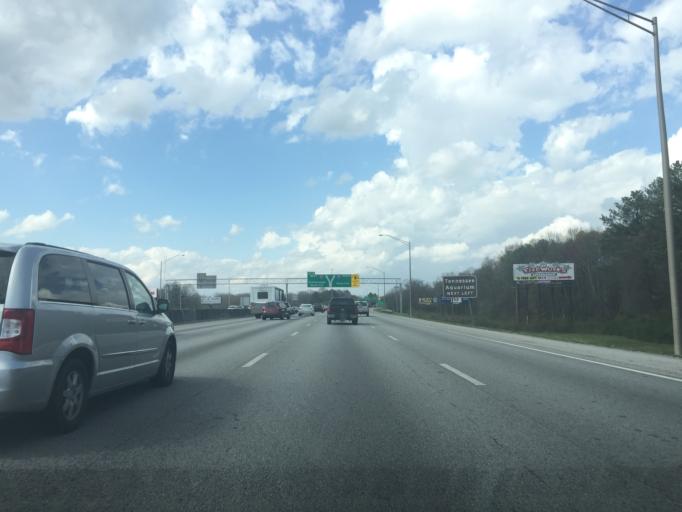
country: US
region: Tennessee
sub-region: Hamilton County
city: East Ridge
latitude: 34.9968
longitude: -85.2083
